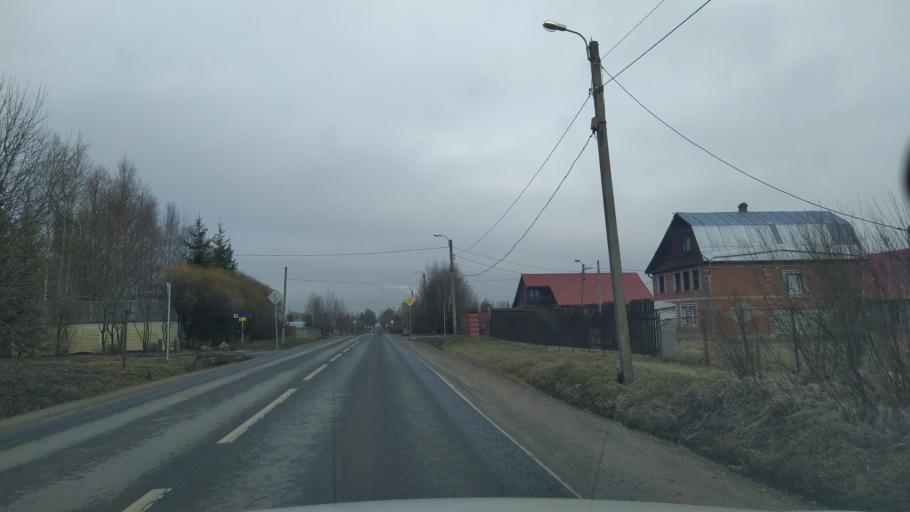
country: RU
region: St.-Petersburg
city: Aleksandrovskaya
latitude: 59.7223
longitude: 30.3463
